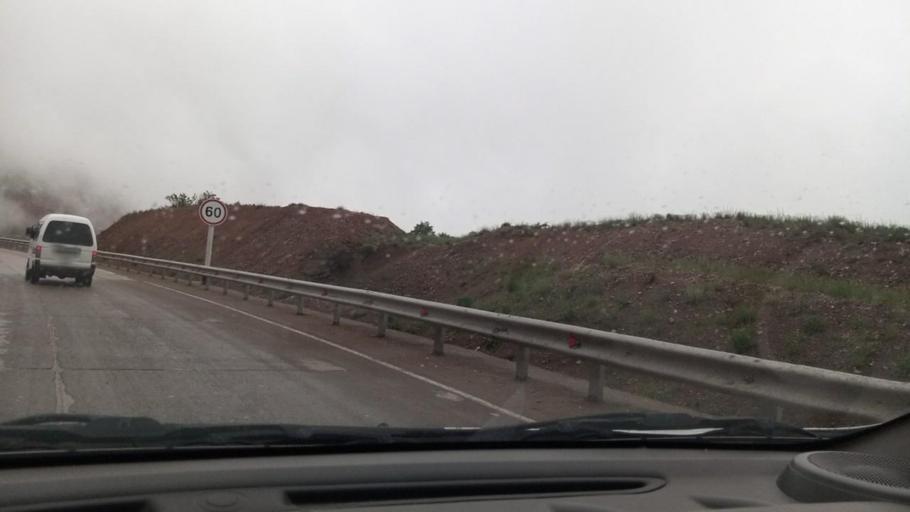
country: UZ
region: Toshkent
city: Angren
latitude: 41.1111
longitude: 70.5035
